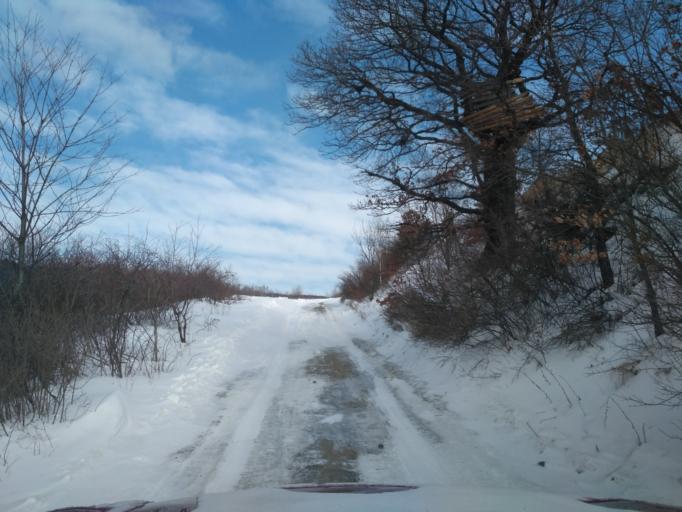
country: SK
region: Kosicky
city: Kosice
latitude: 48.7503
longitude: 21.1230
